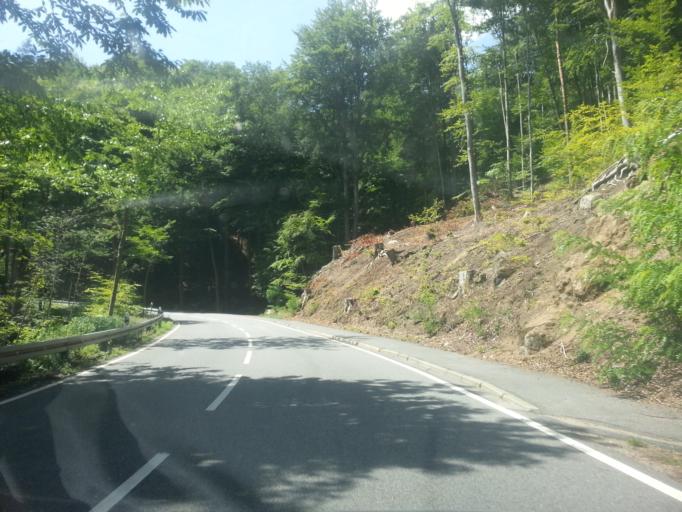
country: DE
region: Hesse
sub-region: Regierungsbezirk Darmstadt
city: Lindenfels
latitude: 49.6873
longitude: 8.7928
